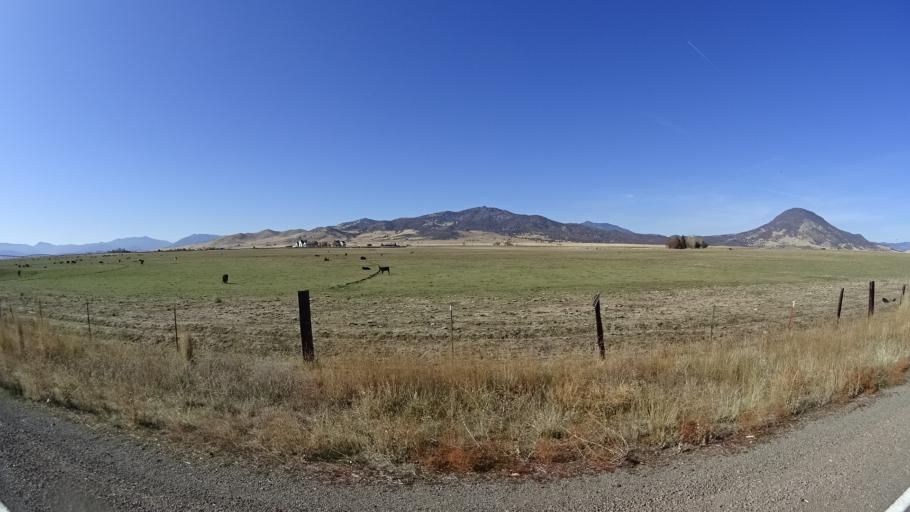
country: US
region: California
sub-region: Siskiyou County
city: Montague
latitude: 41.7906
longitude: -122.4719
